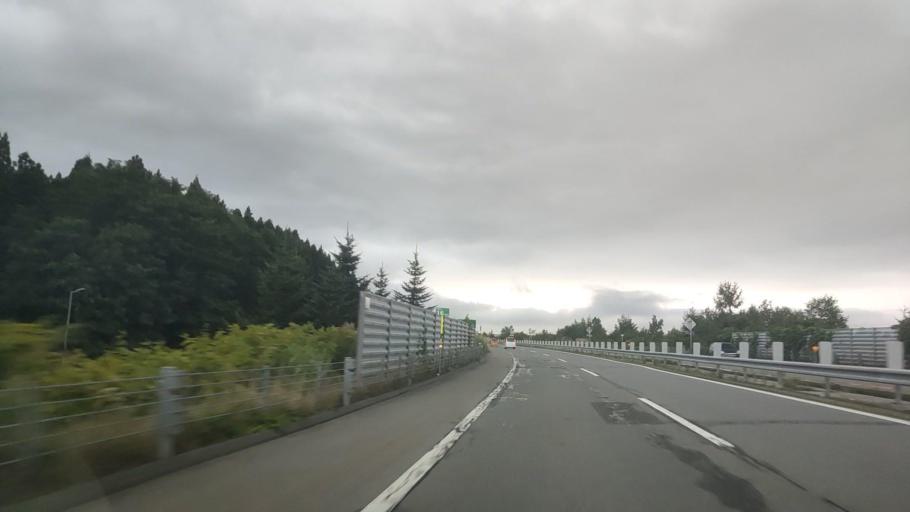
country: JP
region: Hokkaido
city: Nanae
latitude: 41.9043
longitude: 140.6982
